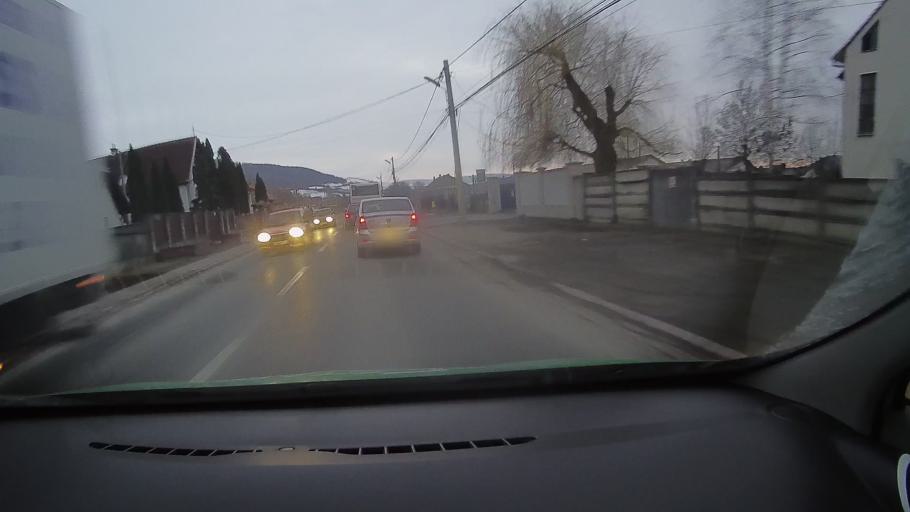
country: RO
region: Harghita
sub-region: Municipiul Odorheiu Secuiesc
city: Odorheiu Secuiesc
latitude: 46.2892
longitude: 25.2900
